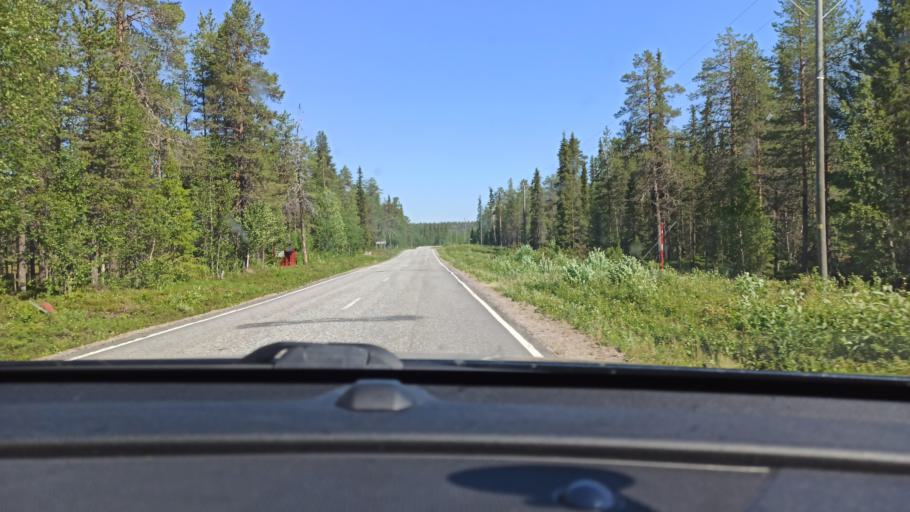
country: FI
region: Lapland
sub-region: Tunturi-Lappi
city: Kolari
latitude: 67.6266
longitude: 24.1555
